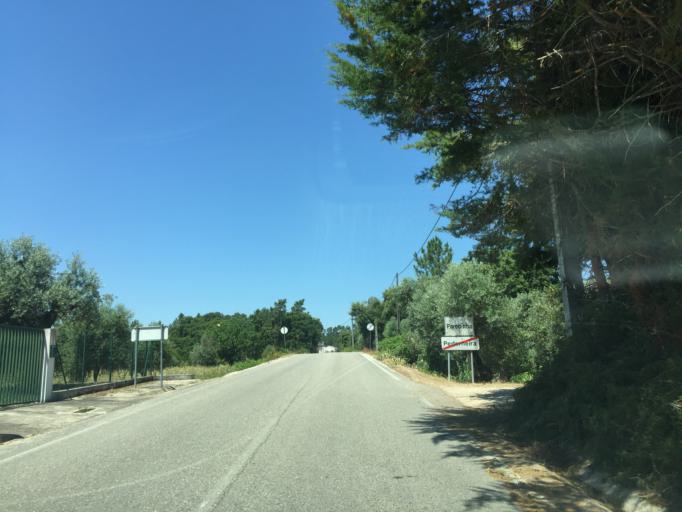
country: PT
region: Santarem
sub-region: Ferreira do Zezere
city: Ferreira do Zezere
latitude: 39.5938
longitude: -8.2794
